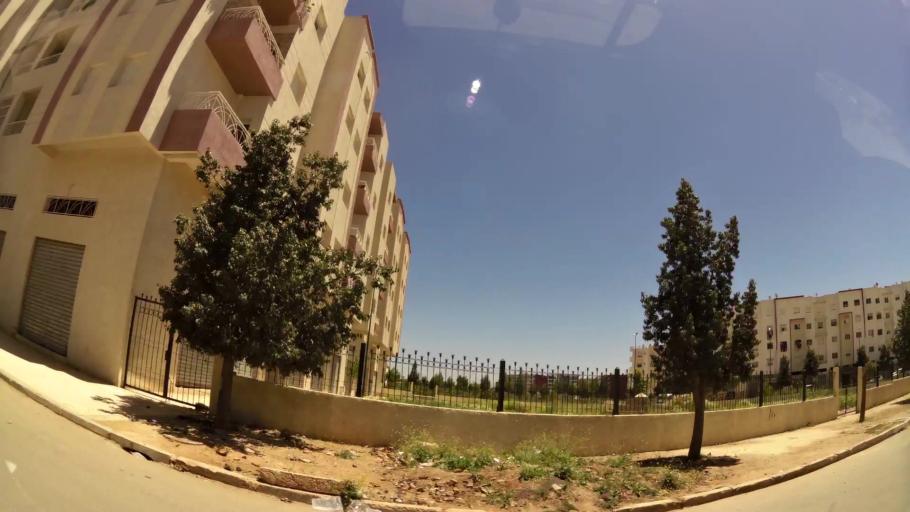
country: MA
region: Meknes-Tafilalet
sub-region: Meknes
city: Meknes
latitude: 33.8627
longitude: -5.5620
